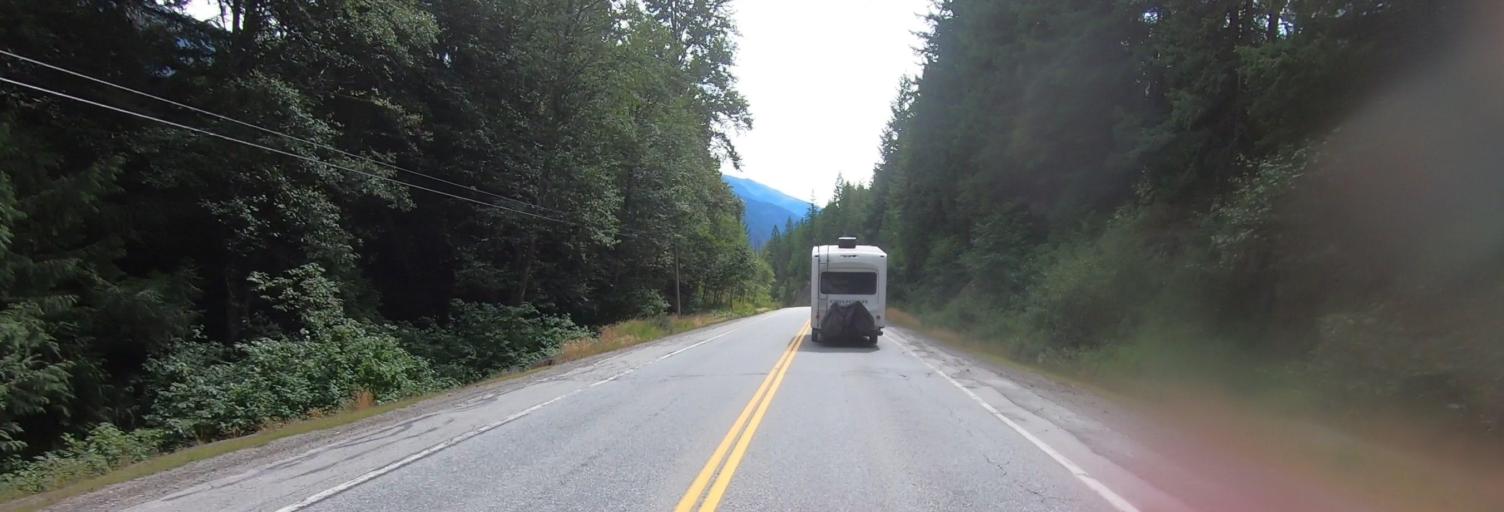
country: CA
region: British Columbia
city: Pemberton
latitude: 50.2614
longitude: -122.8651
